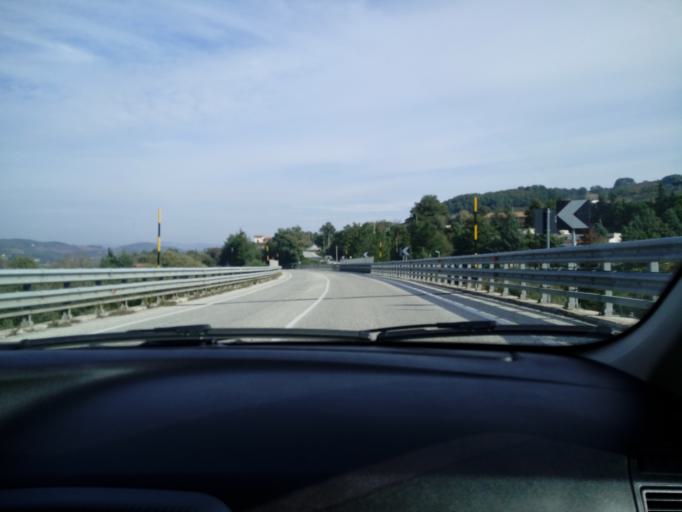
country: IT
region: Molise
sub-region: Provincia di Campobasso
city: Riccia
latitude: 41.4831
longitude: 14.8407
